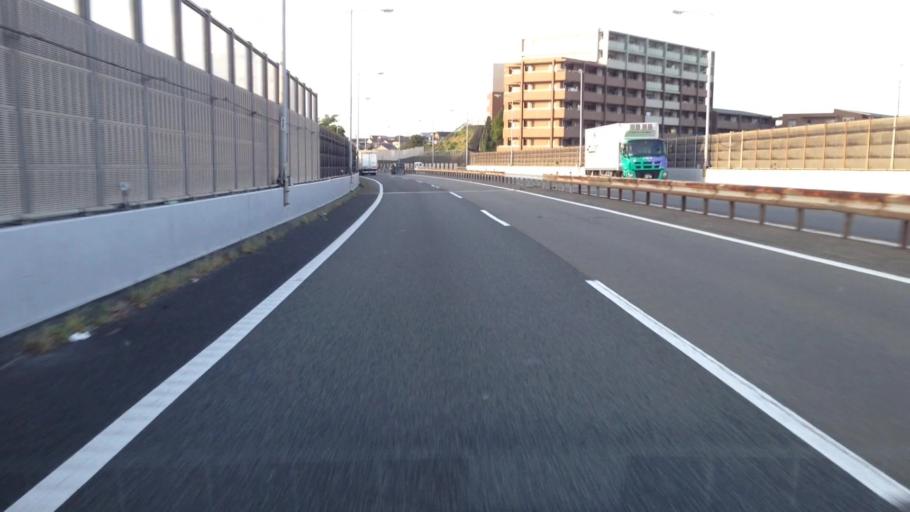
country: JP
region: Kanagawa
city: Yokohama
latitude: 35.3984
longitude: 139.5754
